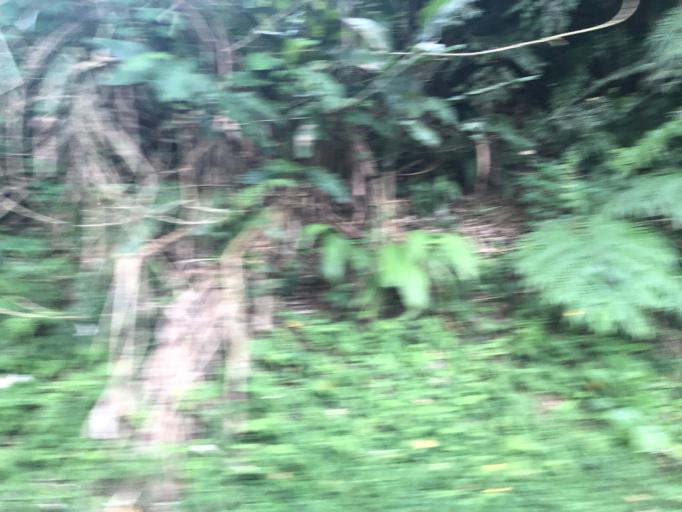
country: TW
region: Taiwan
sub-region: Taoyuan
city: Taoyuan
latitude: 24.9228
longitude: 121.3808
